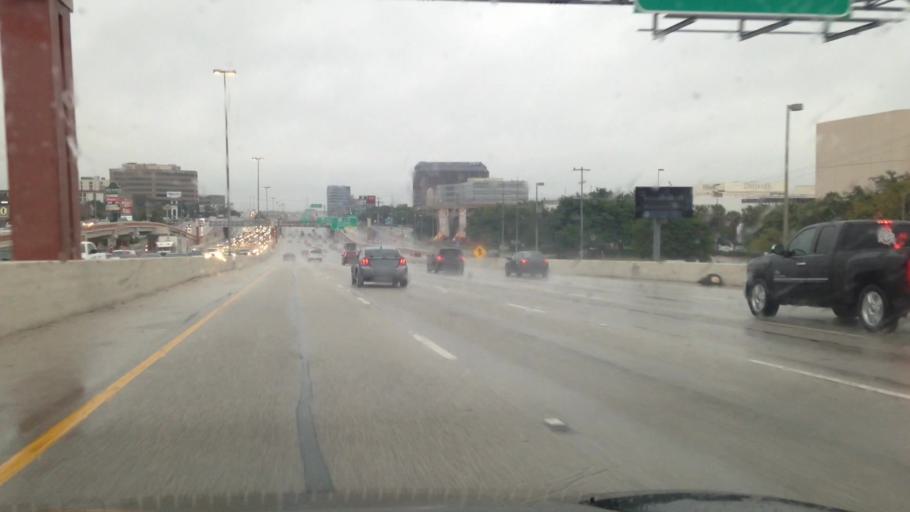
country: US
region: Texas
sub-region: Bexar County
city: Castle Hills
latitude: 29.5205
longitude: -98.4970
